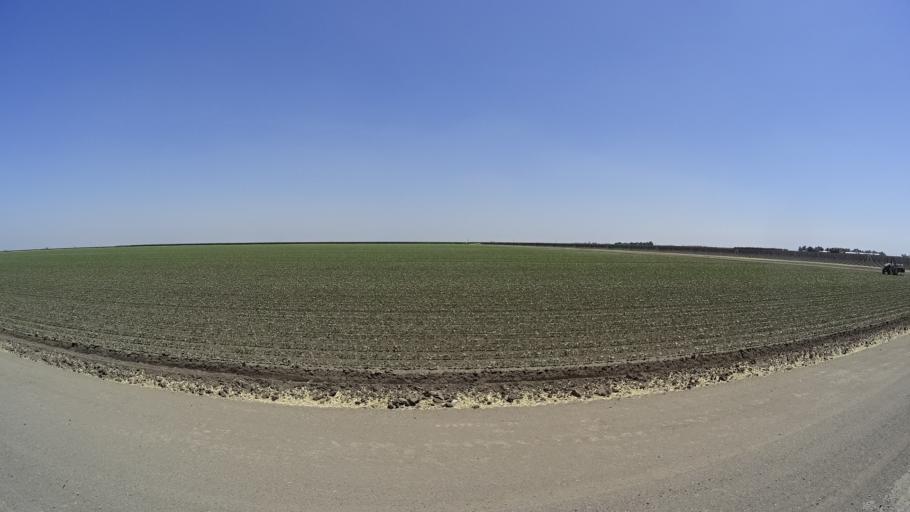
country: US
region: California
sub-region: Kings County
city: Corcoran
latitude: 36.1241
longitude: -119.6444
